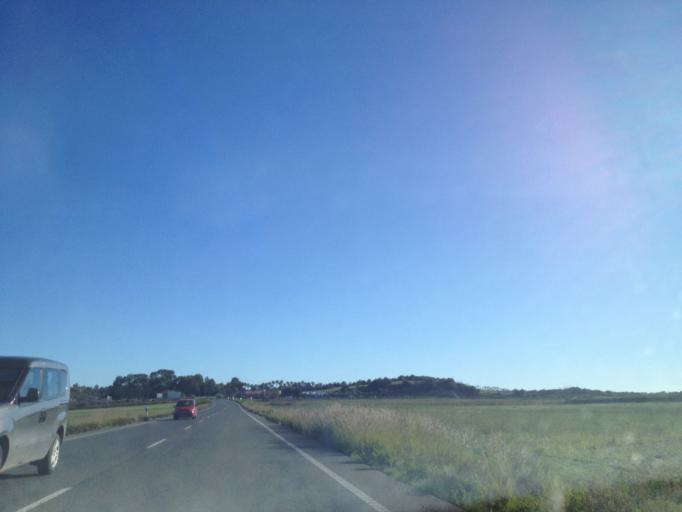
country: ES
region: Balearic Islands
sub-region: Illes Balears
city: Ariany
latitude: 39.6459
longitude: 3.0936
